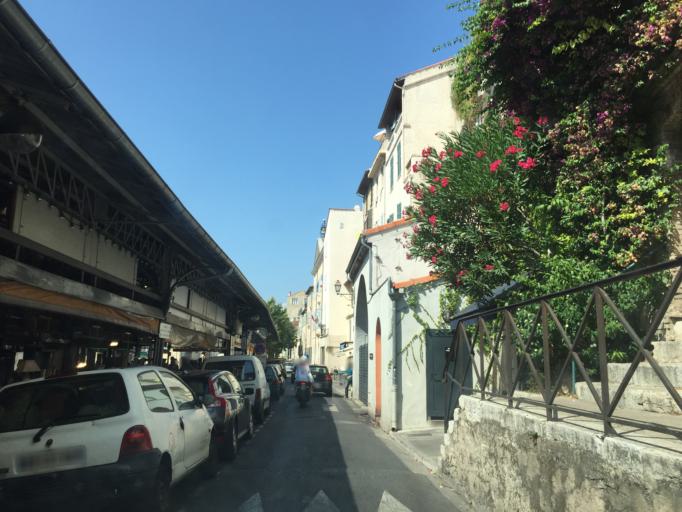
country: FR
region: Provence-Alpes-Cote d'Azur
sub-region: Departement des Alpes-Maritimes
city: Antibes
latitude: 43.5807
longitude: 7.1275
